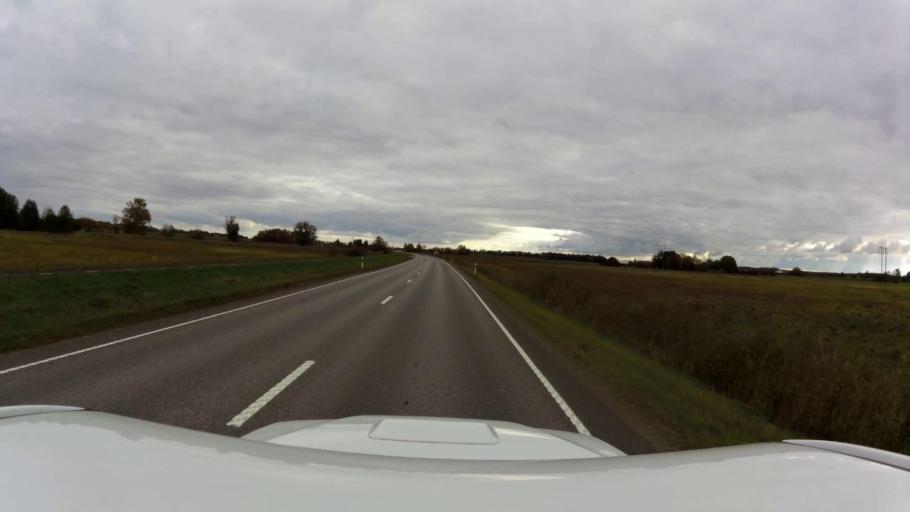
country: SE
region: OEstergoetland
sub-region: Linkopings Kommun
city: Berg
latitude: 58.4561
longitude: 15.5489
